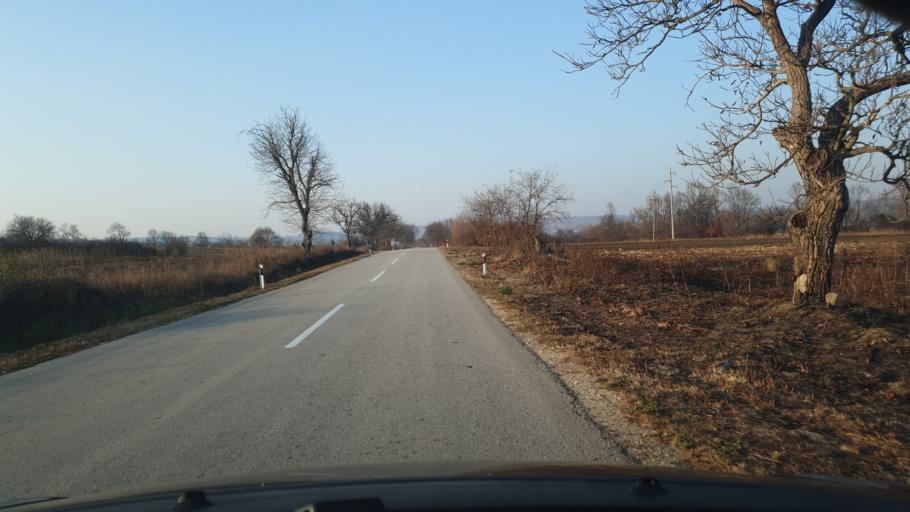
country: RS
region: Central Serbia
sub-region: Zajecarski Okrug
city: Zajecar
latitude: 43.9856
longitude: 22.2866
